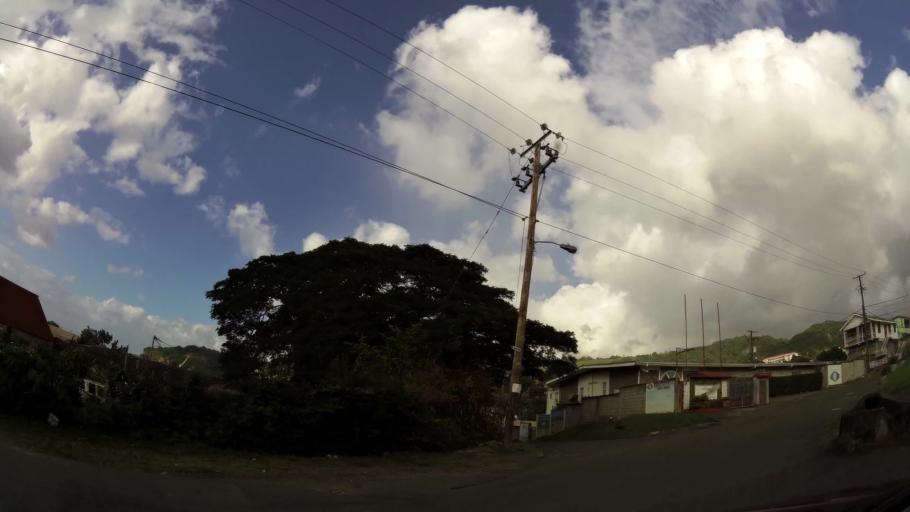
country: DM
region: Saint George
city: Roseau
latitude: 15.3058
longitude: -61.3879
